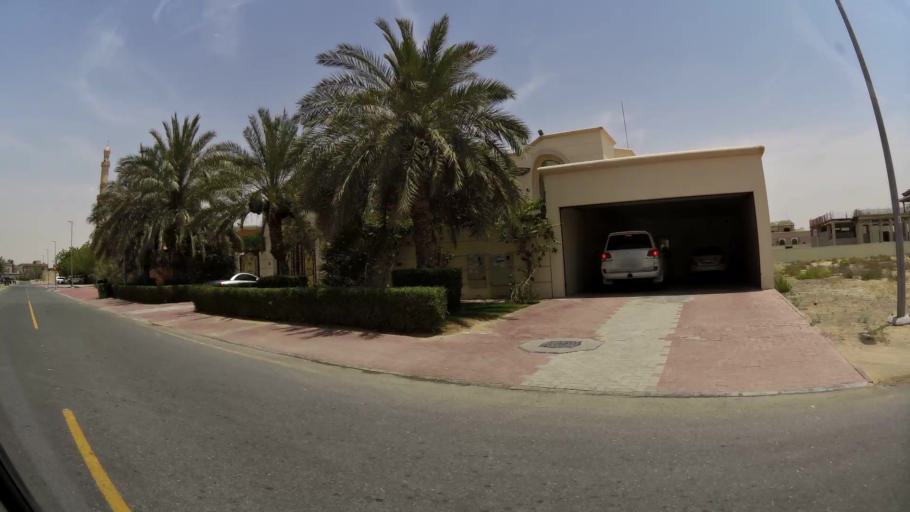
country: AE
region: Ash Shariqah
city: Sharjah
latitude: 25.2523
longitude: 55.4647
